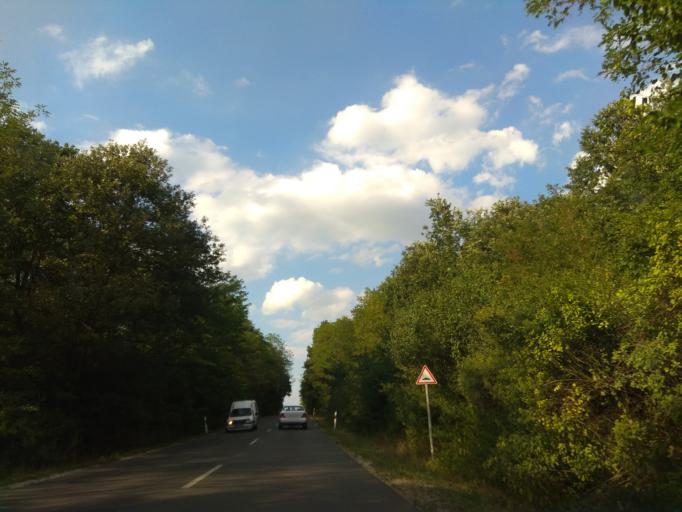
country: HU
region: Borsod-Abauj-Zemplen
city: Harsany
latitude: 47.9830
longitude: 20.7469
